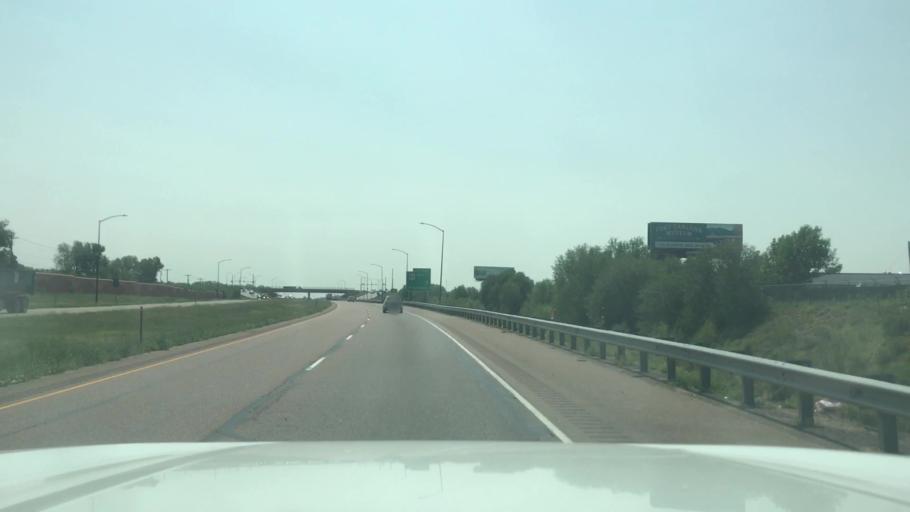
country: US
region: Colorado
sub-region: El Paso County
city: Fountain
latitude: 38.6784
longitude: -104.7133
